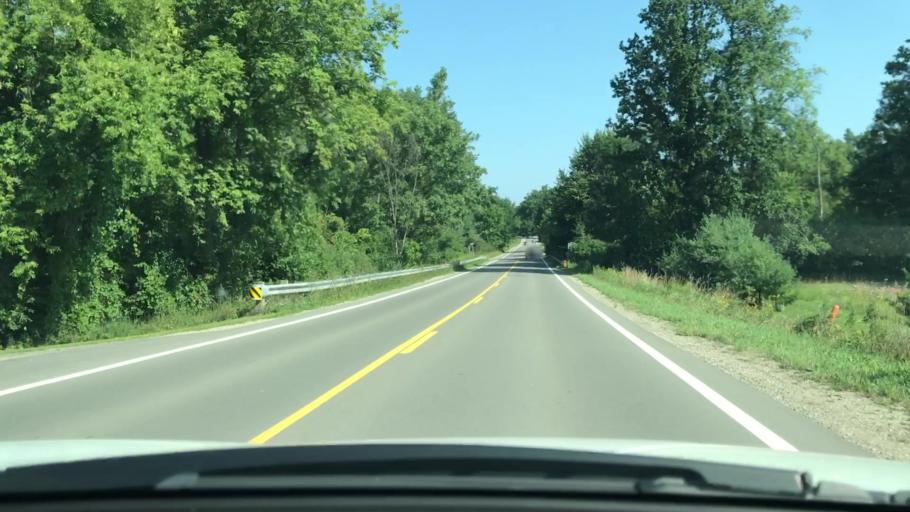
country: US
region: Michigan
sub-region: Oakland County
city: Oxford
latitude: 42.8011
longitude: -83.3333
